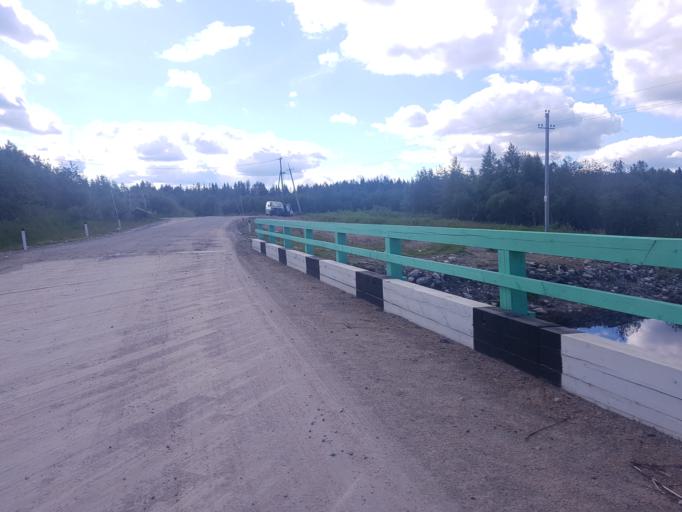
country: RU
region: Republic of Karelia
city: Kostomuksha
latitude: 64.8904
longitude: 30.5280
